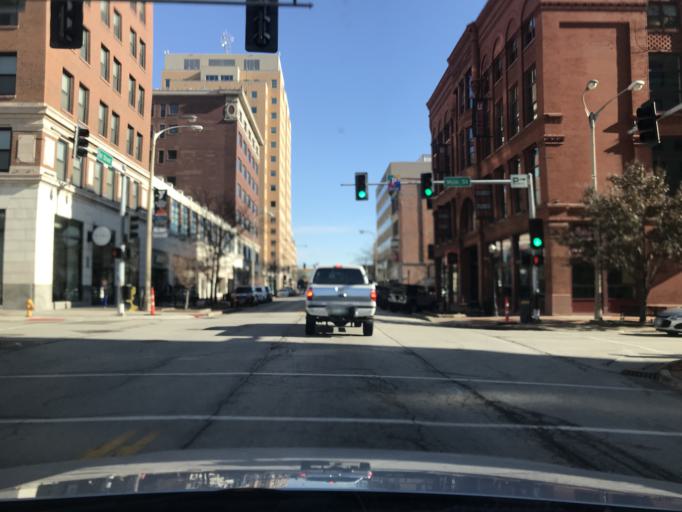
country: US
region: Iowa
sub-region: Scott County
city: Davenport
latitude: 41.5214
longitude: -90.5758
